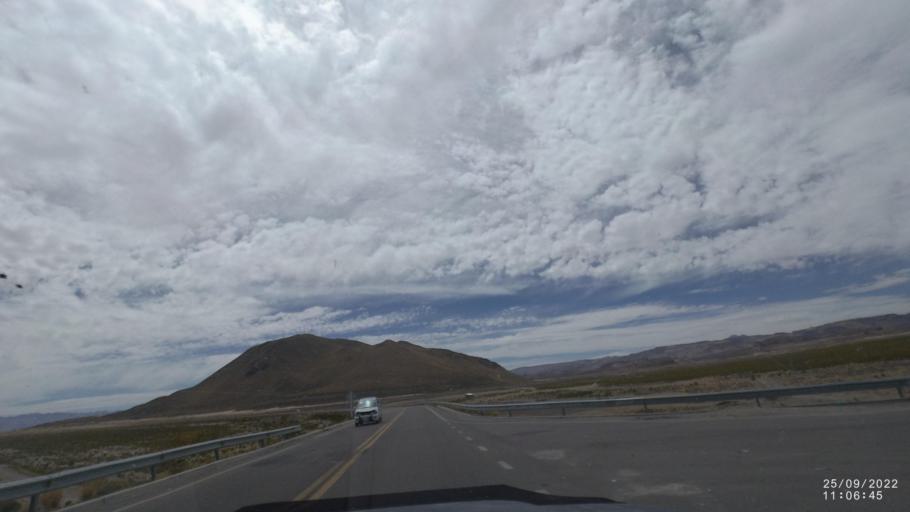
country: BO
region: Oruro
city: Challapata
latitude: -19.3540
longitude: -66.8584
